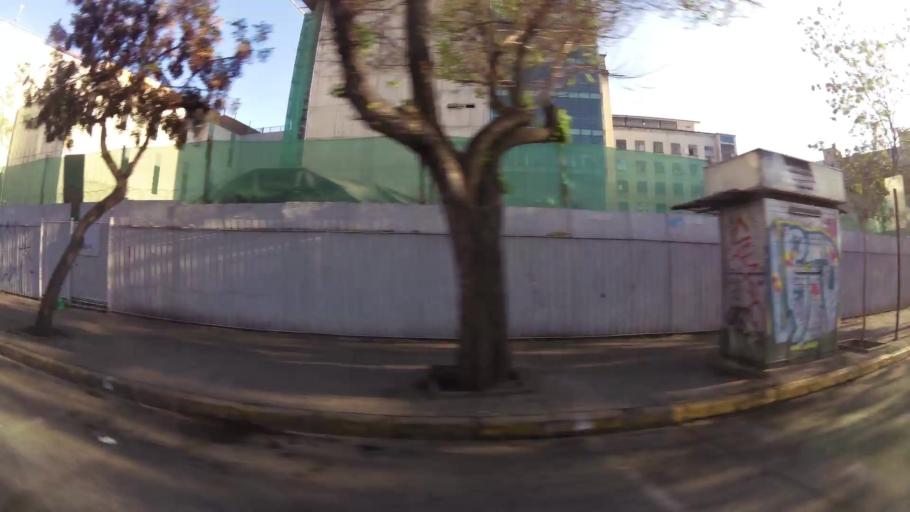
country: CL
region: Santiago Metropolitan
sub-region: Provincia de Santiago
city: Santiago
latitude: -33.4447
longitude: -70.6382
